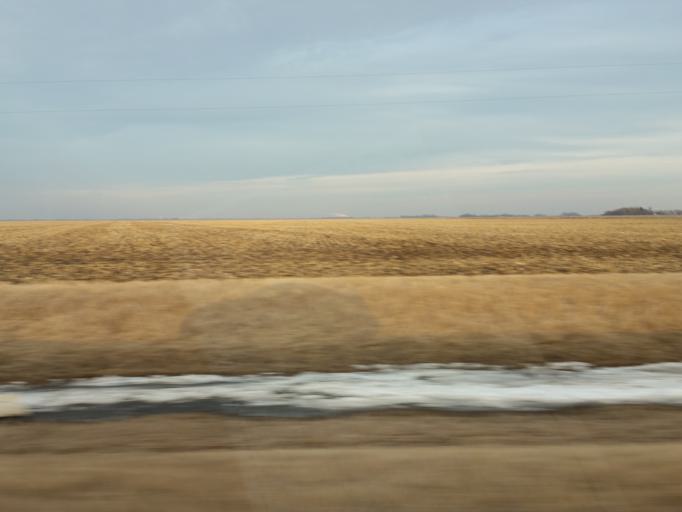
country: US
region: North Dakota
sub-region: Traill County
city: Mayville
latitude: 47.4485
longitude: -97.3260
